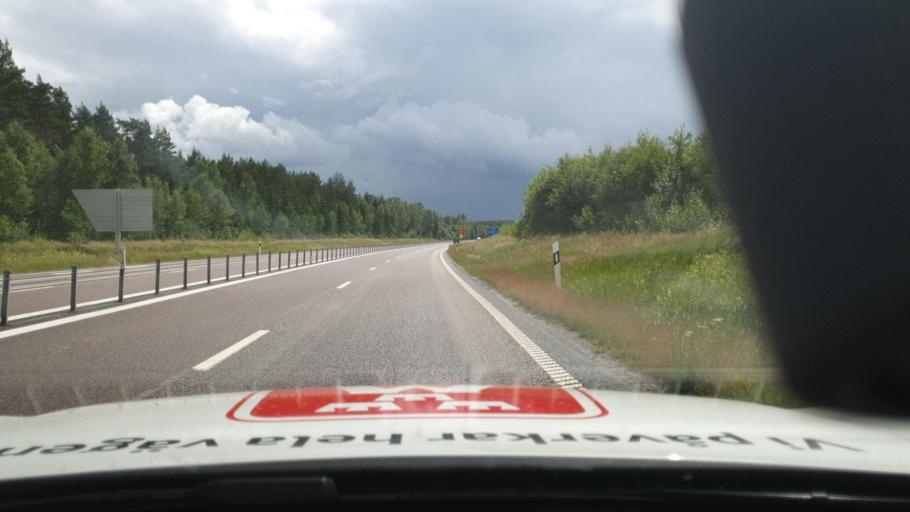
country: SE
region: Vaestra Goetaland
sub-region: Skovde Kommun
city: Skultorp
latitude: 58.3389
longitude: 13.8630
